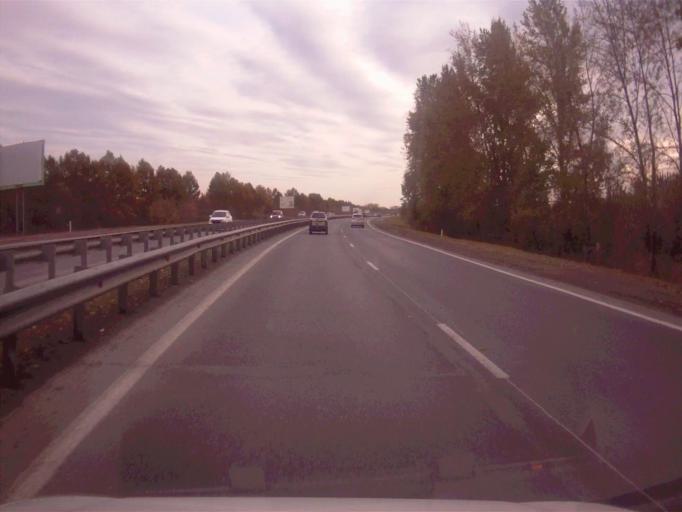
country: RU
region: Chelyabinsk
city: Novosineglazovskiy
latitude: 55.0278
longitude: 61.4493
